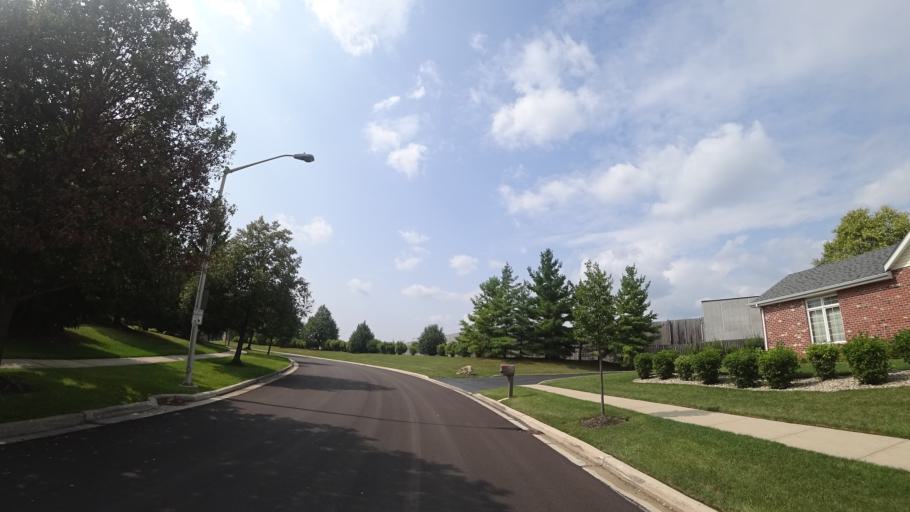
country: US
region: Illinois
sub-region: Cook County
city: Tinley Park
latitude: 41.5990
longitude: -87.7883
